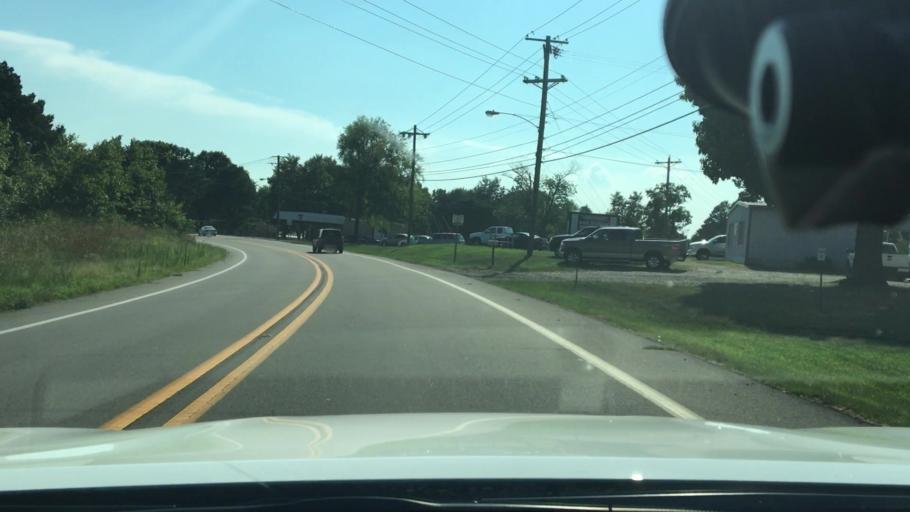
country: US
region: Arkansas
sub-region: Johnson County
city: Clarksville
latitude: 35.4726
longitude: -93.5123
